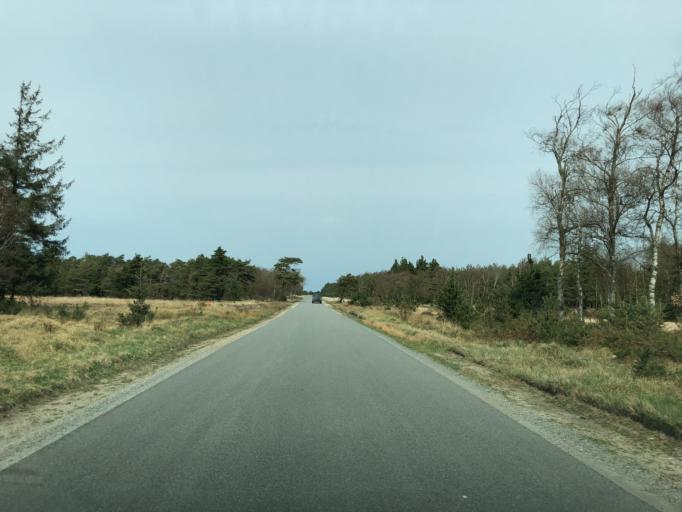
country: DK
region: South Denmark
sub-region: Varde Kommune
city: Oksbol
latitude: 55.6265
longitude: 8.1699
